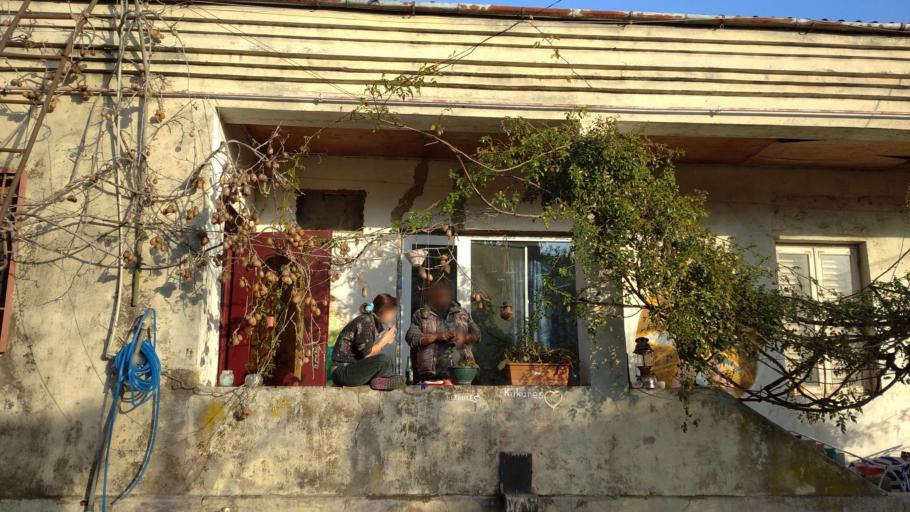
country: GE
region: Samegrelo and Zemo Svaneti
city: P'ot'i
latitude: 42.1447
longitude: 41.6848
